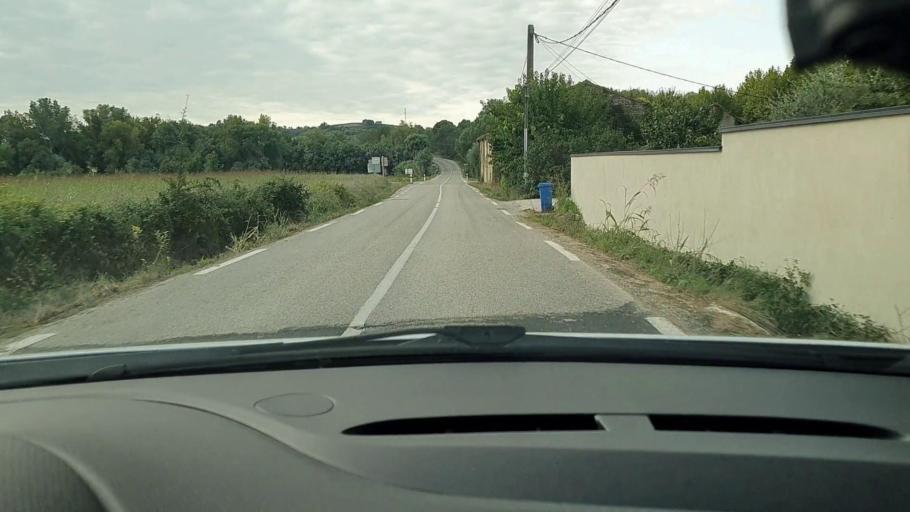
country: FR
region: Languedoc-Roussillon
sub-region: Departement du Gard
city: Mons
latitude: 44.0685
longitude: 4.2226
